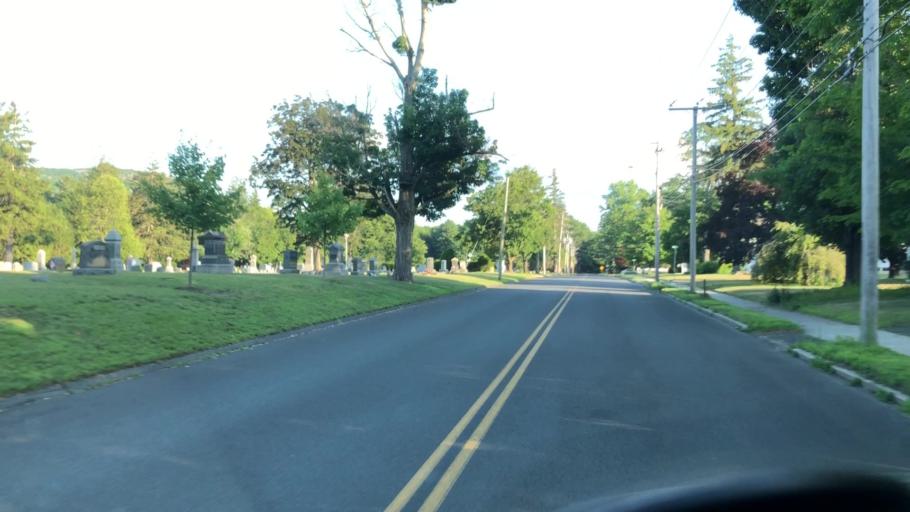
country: US
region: Massachusetts
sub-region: Hampshire County
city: Easthampton
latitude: 42.2631
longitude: -72.6700
